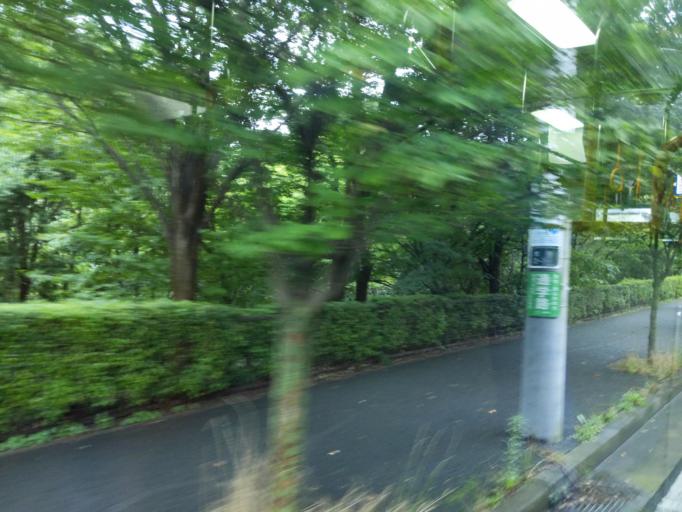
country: JP
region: Tokyo
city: Chofugaoka
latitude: 35.5844
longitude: 139.5624
